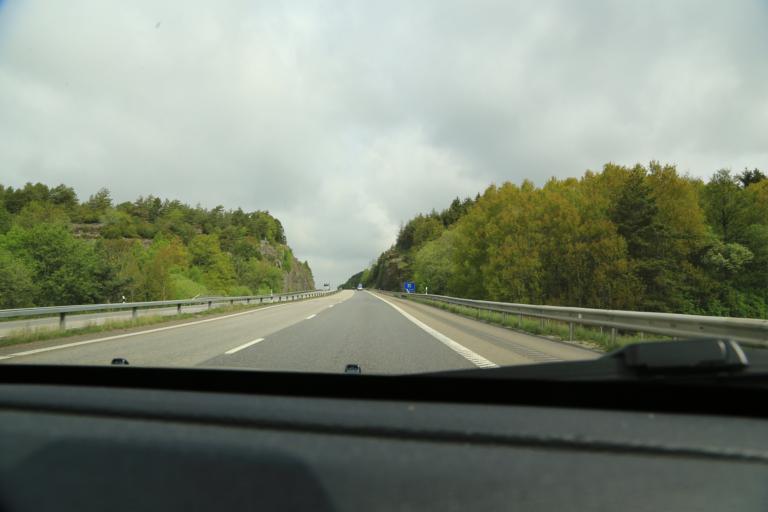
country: SE
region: Halland
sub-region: Kungsbacka Kommun
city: Frillesas
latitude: 57.3047
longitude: 12.2148
